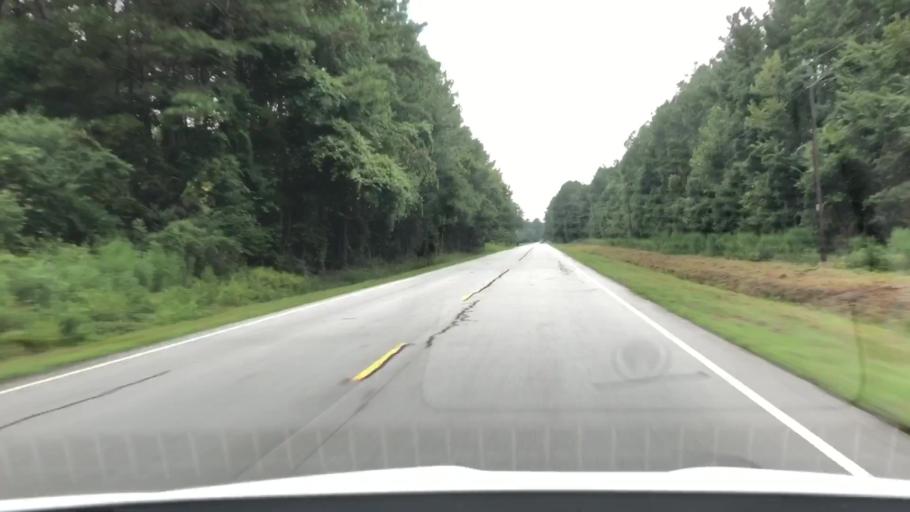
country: US
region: North Carolina
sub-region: Lenoir County
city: Kinston
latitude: 35.1145
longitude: -77.5105
